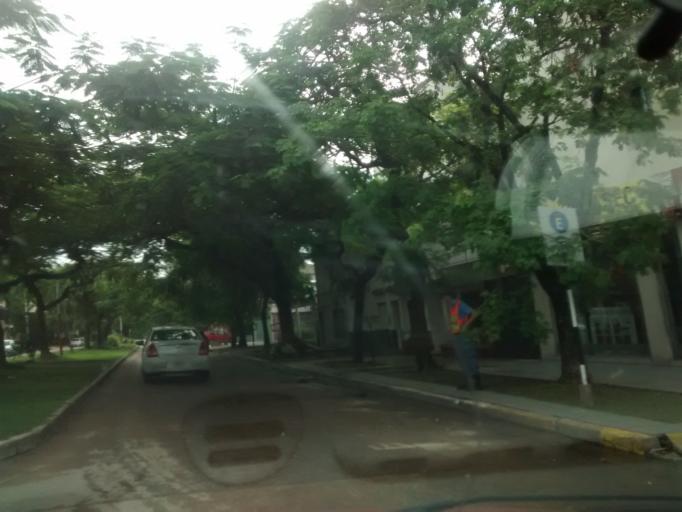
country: AR
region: Chaco
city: Resistencia
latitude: -27.4496
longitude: -58.9935
